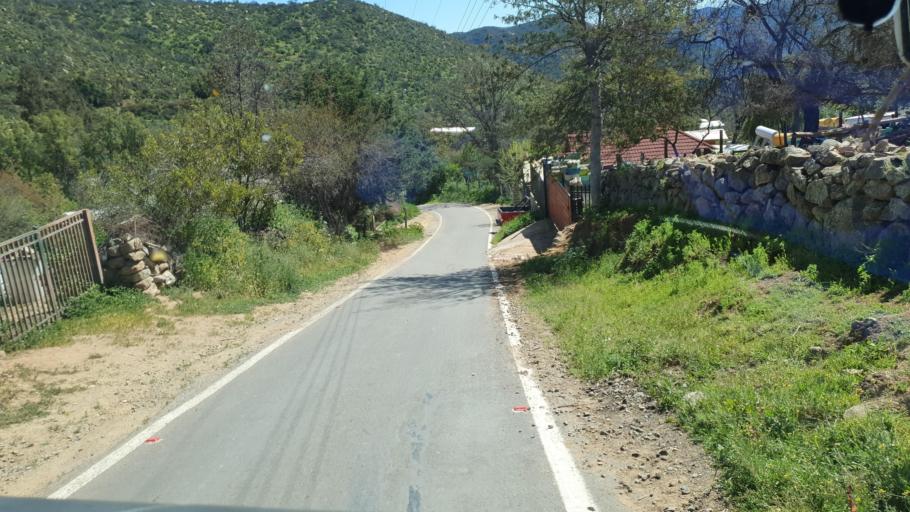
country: CL
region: Santiago Metropolitan
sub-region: Provincia de Chacabuco
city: Lampa
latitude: -33.1947
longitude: -71.0933
